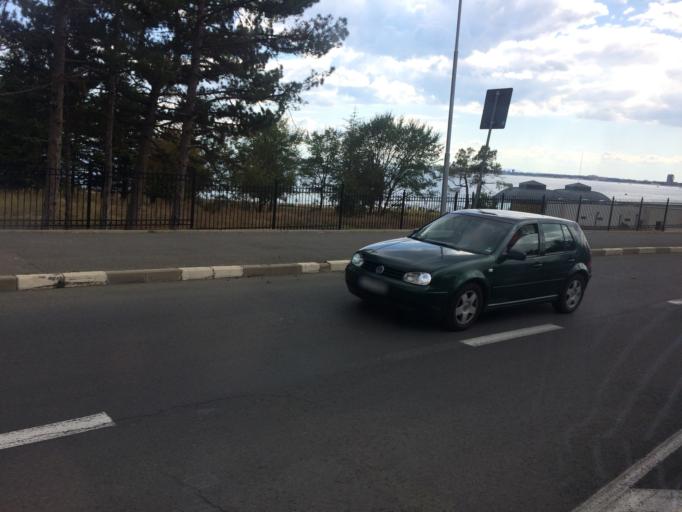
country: BG
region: Burgas
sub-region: Obshtina Nesebur
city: Sveti Vlas
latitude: 42.7106
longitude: 27.7333
